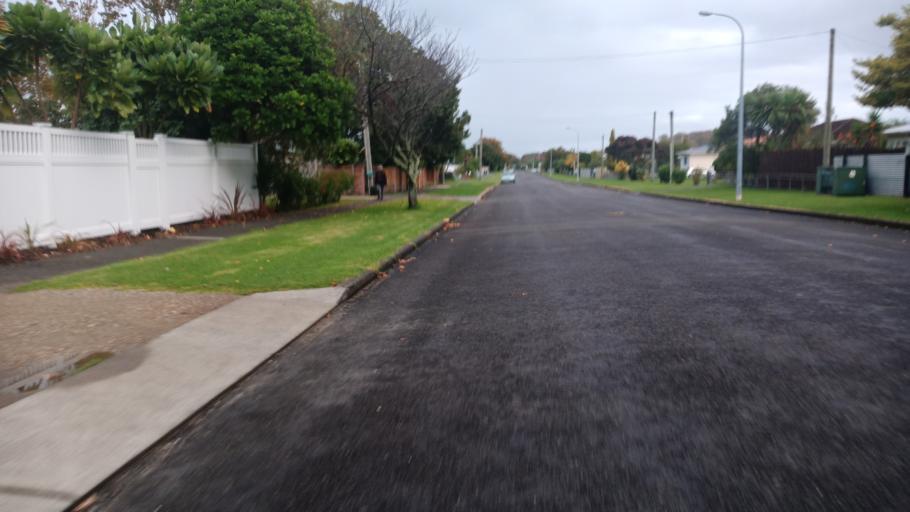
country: NZ
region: Gisborne
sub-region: Gisborne District
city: Gisborne
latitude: -38.6439
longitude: 178.0140
